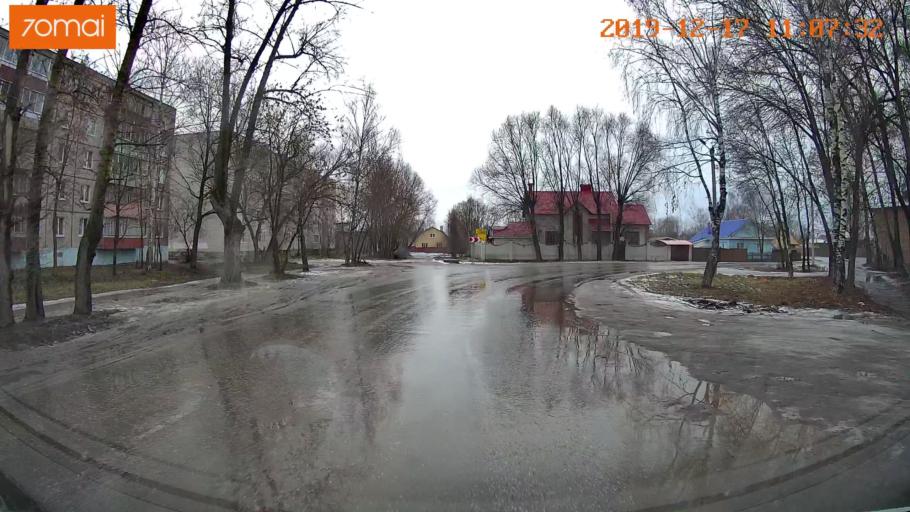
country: RU
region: Vladimir
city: Gus'-Khrustal'nyy
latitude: 55.6101
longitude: 40.6445
